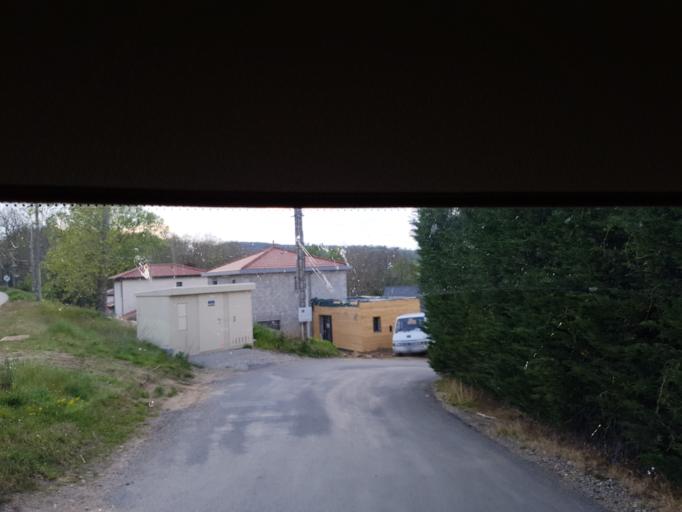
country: FR
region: Rhone-Alpes
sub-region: Departement du Rhone
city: Lentilly
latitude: 45.8054
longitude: 4.6535
